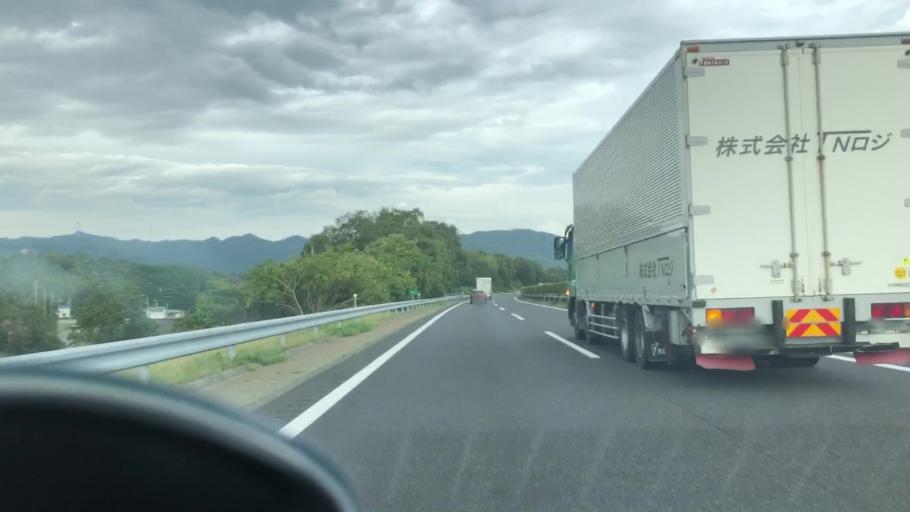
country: JP
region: Hyogo
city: Yashiro
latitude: 34.9327
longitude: 134.9168
